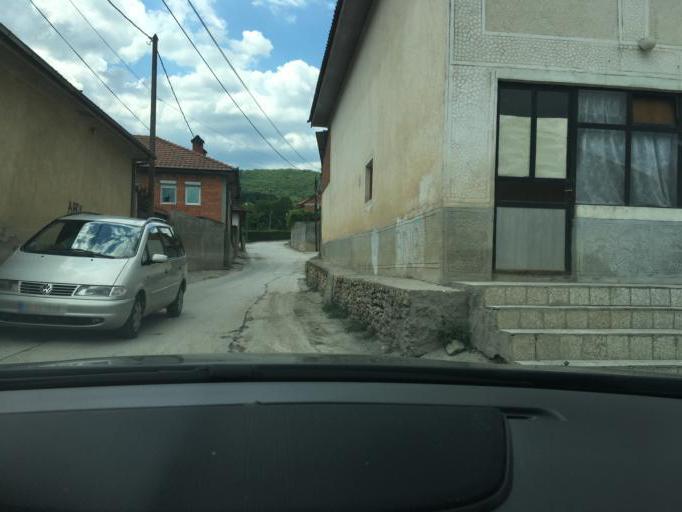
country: MK
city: Ljubin
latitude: 41.9798
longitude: 21.3056
